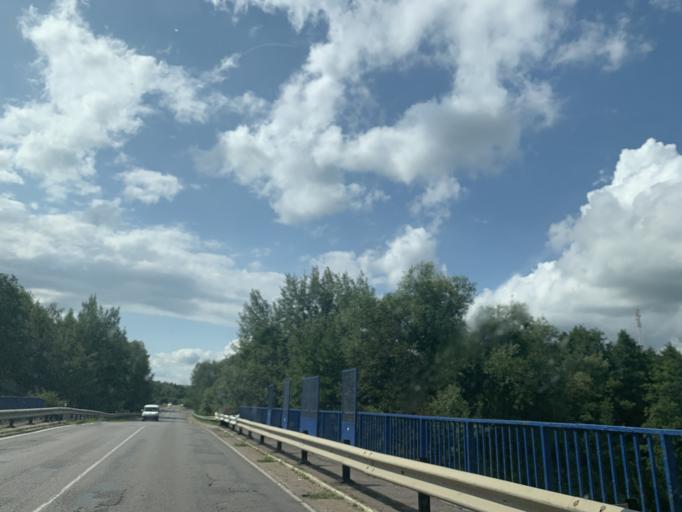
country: BY
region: Minsk
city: Enyerhyetykaw
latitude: 53.5890
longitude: 27.0472
